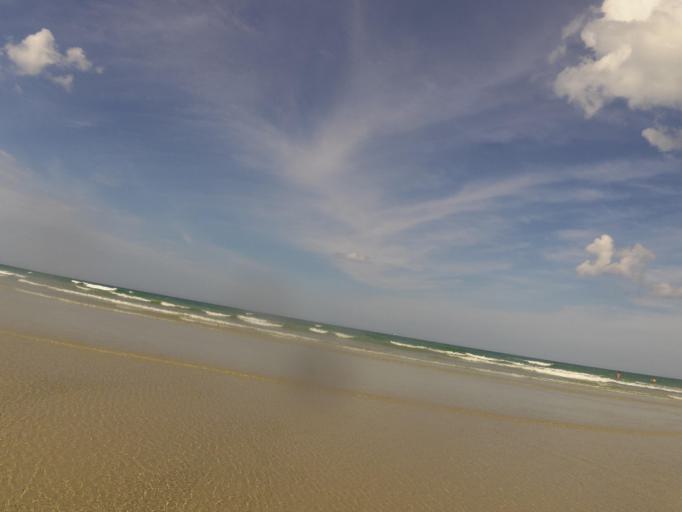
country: US
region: Florida
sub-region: Volusia County
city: Ponce Inlet
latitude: 29.0946
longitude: -80.9321
